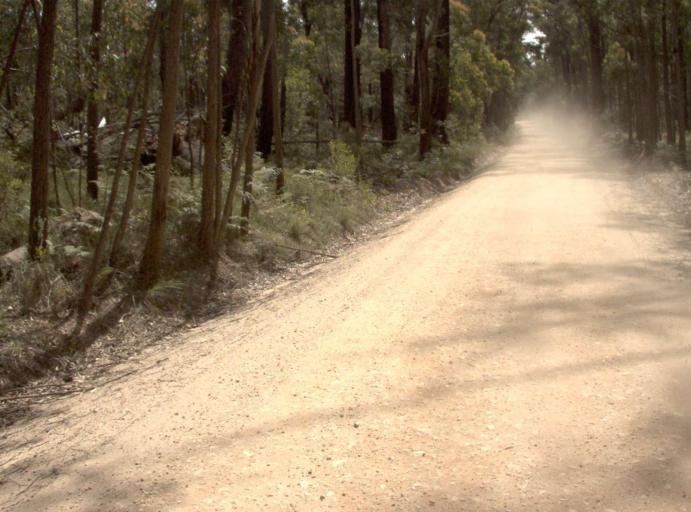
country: AU
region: Victoria
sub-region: East Gippsland
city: Lakes Entrance
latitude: -37.6569
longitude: 148.6451
